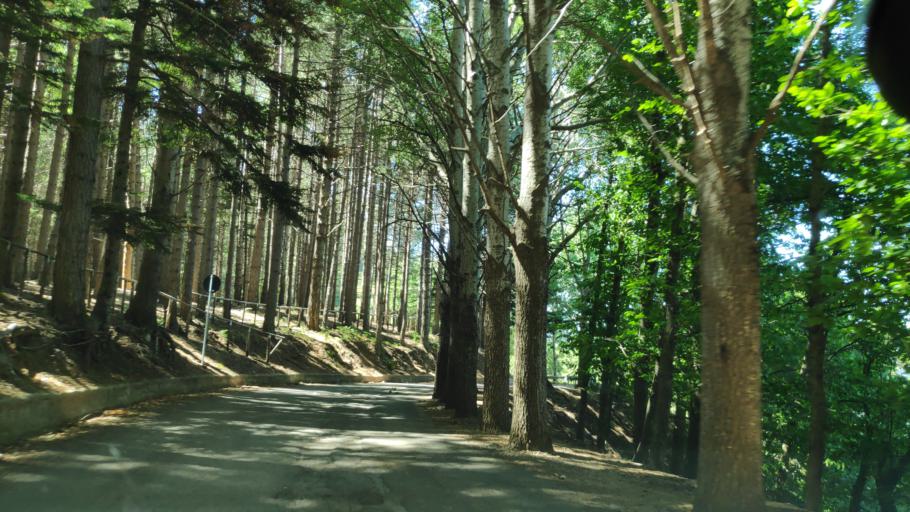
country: IT
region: Calabria
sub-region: Provincia di Reggio Calabria
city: Africo Vecchio
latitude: 38.0379
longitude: 15.9517
